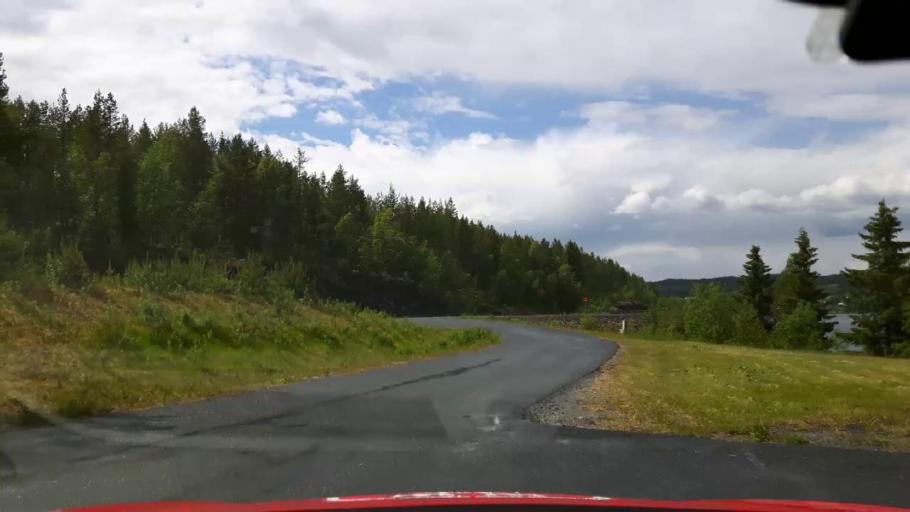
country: SE
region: Jaemtland
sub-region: Krokoms Kommun
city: Valla
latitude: 63.8986
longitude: 14.2474
